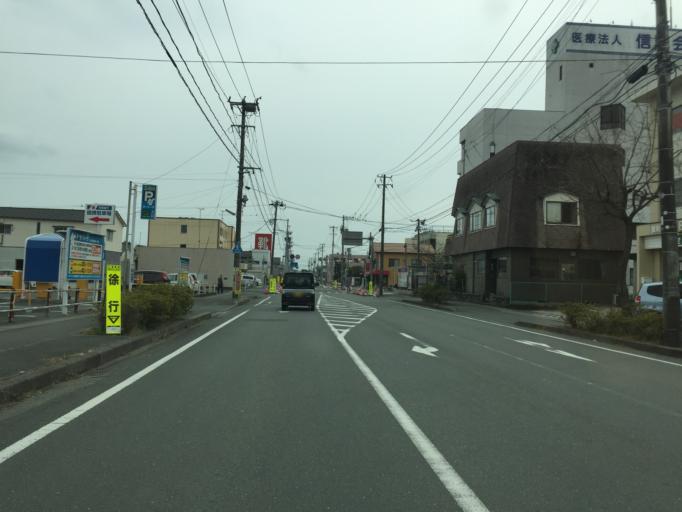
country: JP
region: Ibaraki
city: Kitaibaraki
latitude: 36.9180
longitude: 140.7998
